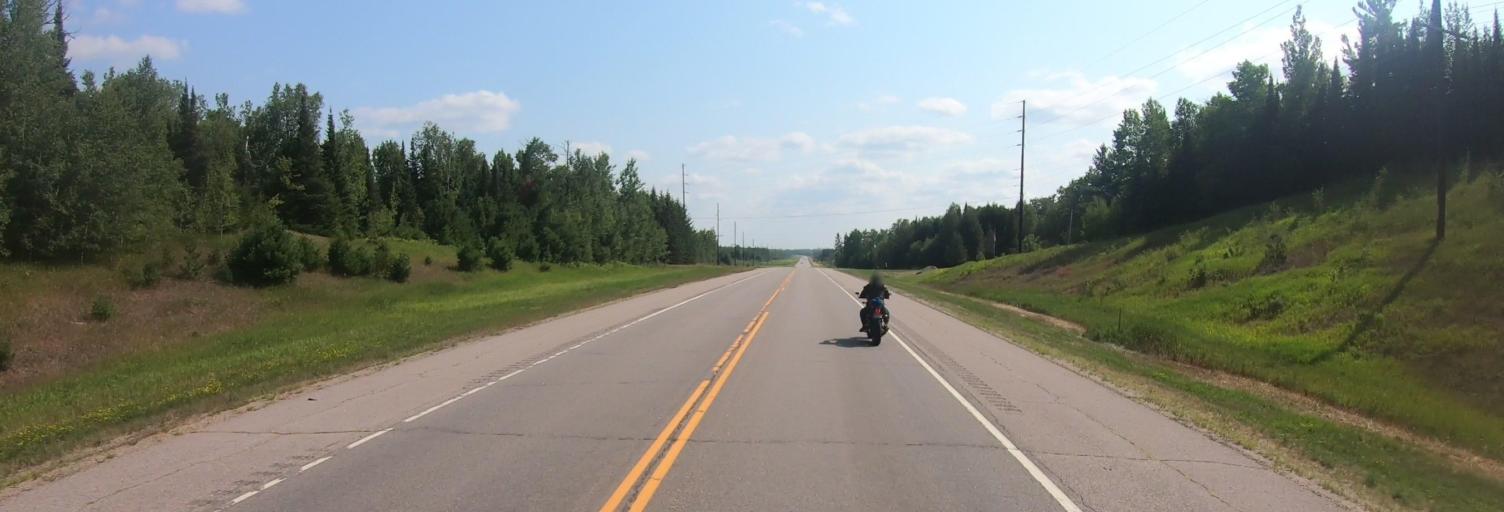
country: US
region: Minnesota
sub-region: Saint Louis County
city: Chisholm
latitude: 47.9557
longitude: -92.8292
